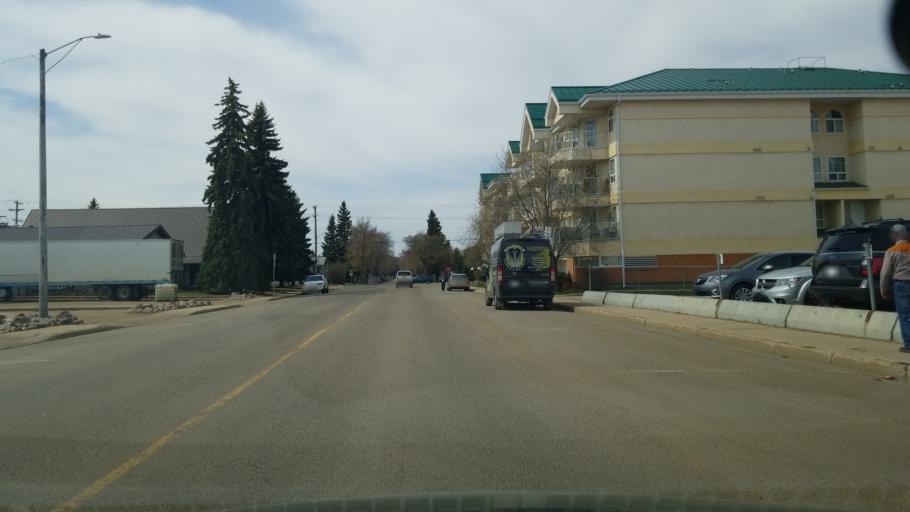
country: CA
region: Saskatchewan
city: Lloydminster
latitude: 53.2825
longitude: -110.0088
